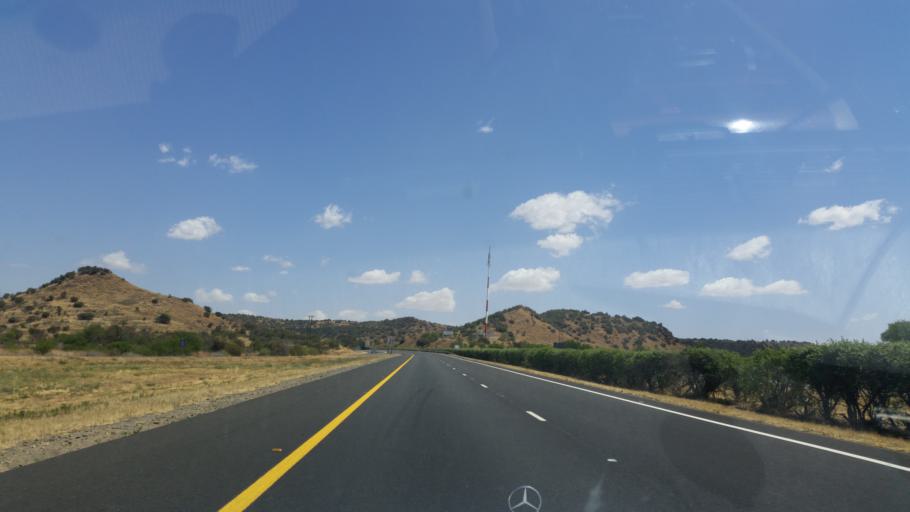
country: ZA
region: Orange Free State
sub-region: Mangaung Metropolitan Municipality
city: Bloemfontein
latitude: -28.9783
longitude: 26.2880
